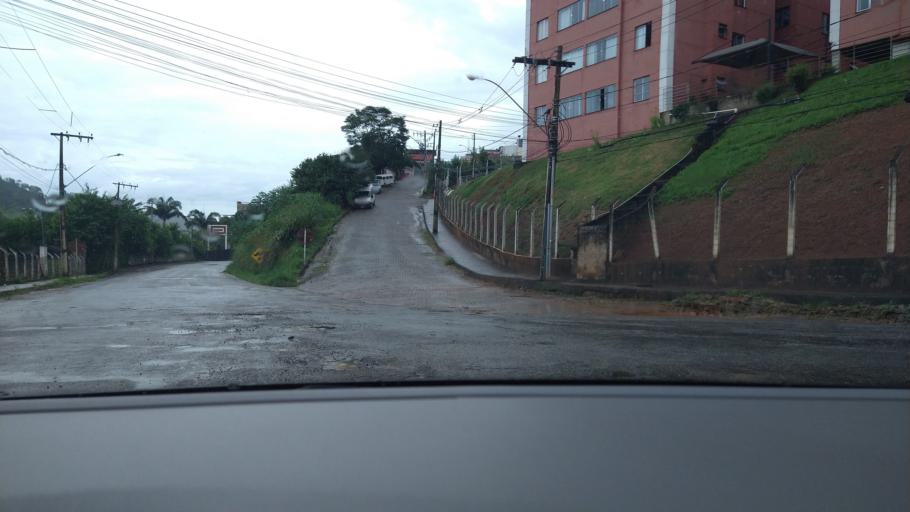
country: BR
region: Minas Gerais
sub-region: Ponte Nova
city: Ponte Nova
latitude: -20.3987
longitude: -42.9005
